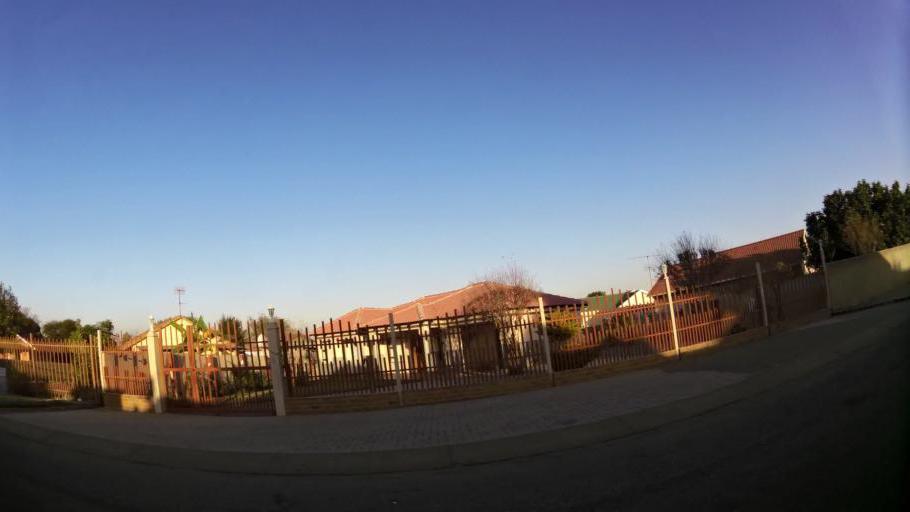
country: ZA
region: North-West
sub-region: Bojanala Platinum District Municipality
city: Rustenburg
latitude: -25.6382
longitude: 27.2055
